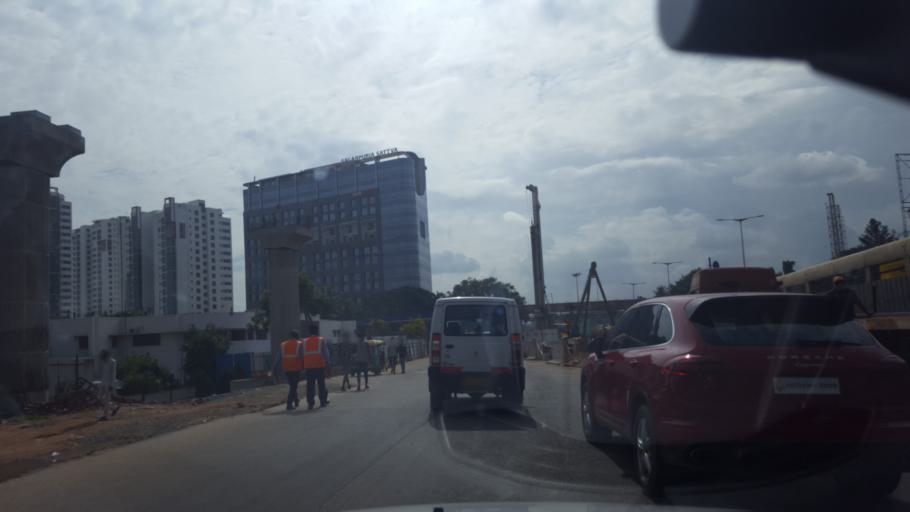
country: IN
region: Karnataka
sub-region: Bangalore Urban
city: Bangalore
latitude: 12.9974
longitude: 77.6710
